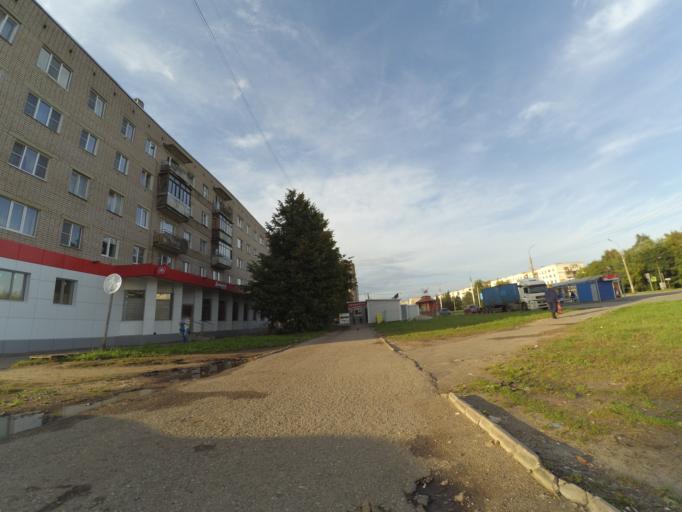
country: RU
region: Novgorod
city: Pankovka
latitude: 58.5266
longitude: 31.2297
